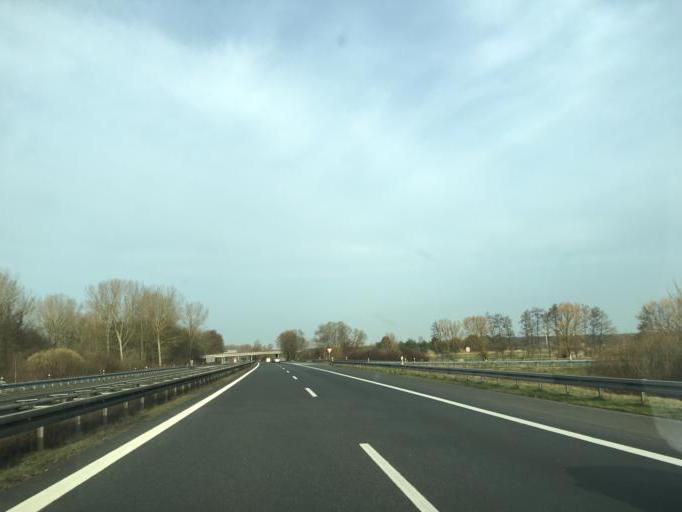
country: DE
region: Brandenburg
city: Leegebruch
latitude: 52.7048
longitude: 13.2002
